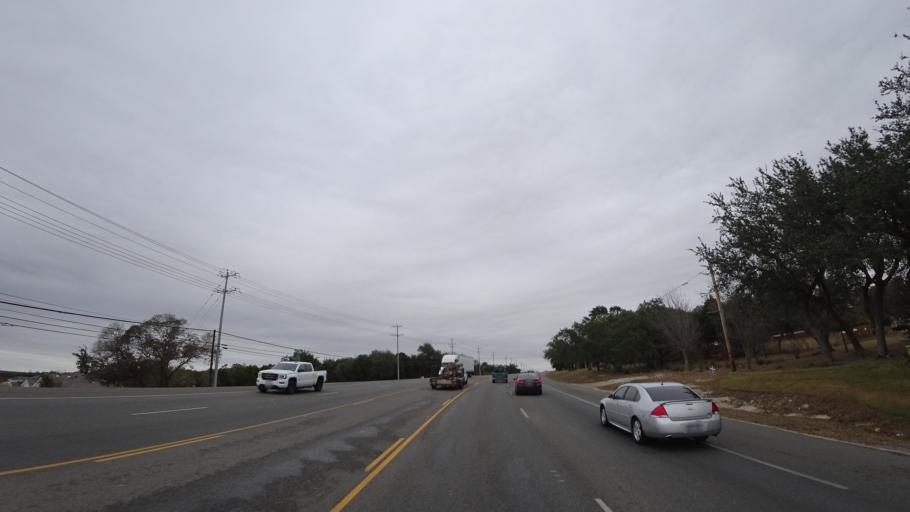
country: US
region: Texas
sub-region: Williamson County
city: Anderson Mill
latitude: 30.4349
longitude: -97.8404
